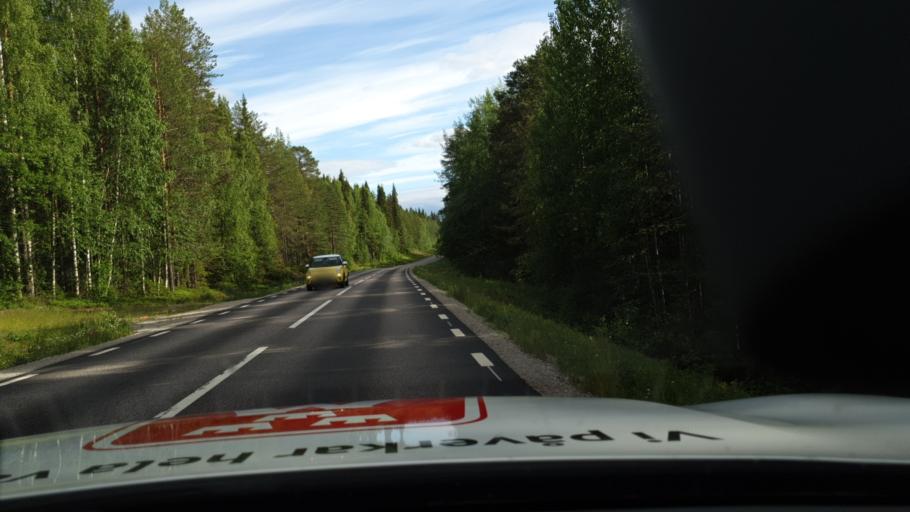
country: SE
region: Norrbotten
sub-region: Overkalix Kommun
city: OEverkalix
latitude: 66.4702
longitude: 22.7919
